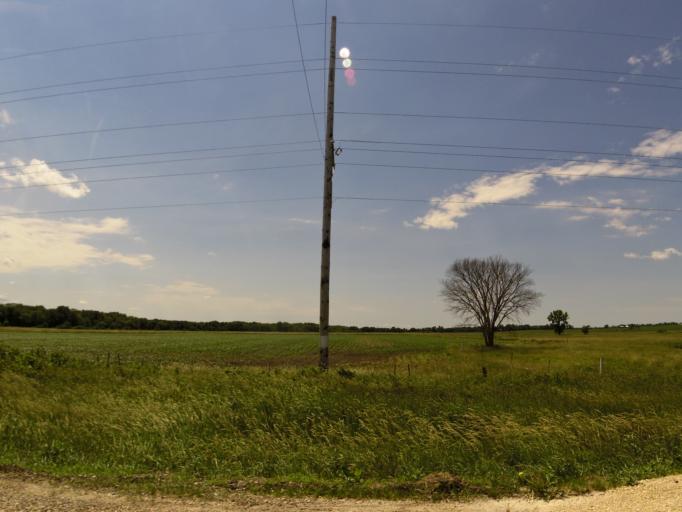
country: US
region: Iowa
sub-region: Bremer County
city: Tripoli
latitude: 42.7148
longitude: -92.1817
